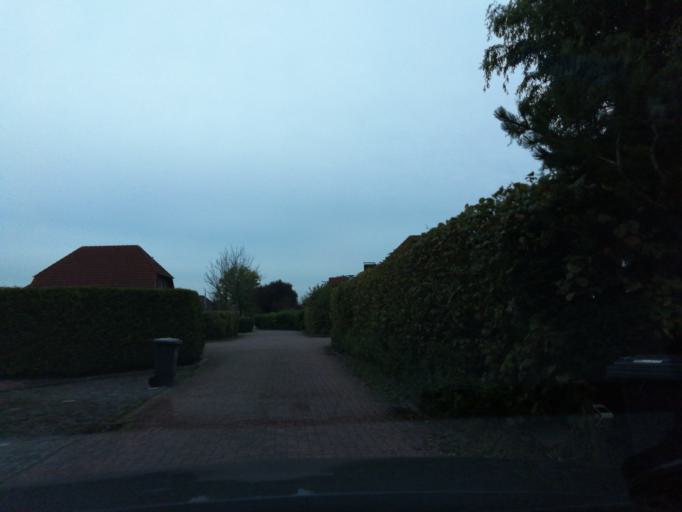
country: DE
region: Lower Saxony
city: Schillig
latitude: 53.6367
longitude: 8.0347
